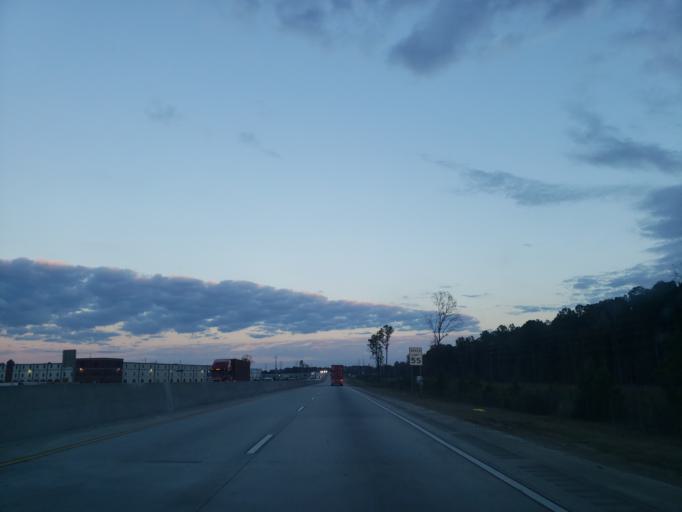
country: US
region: Georgia
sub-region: Chatham County
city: Port Wentworth
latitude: 32.1431
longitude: -81.1701
